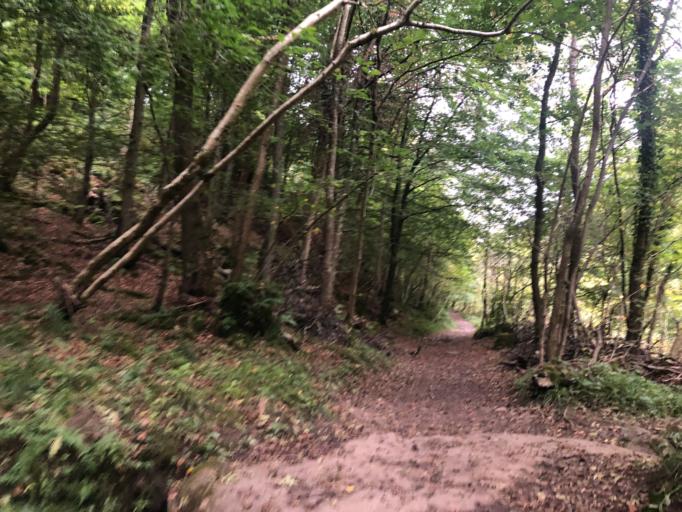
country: GB
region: Scotland
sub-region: Perth and Kinross
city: Pitlochry
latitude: 56.7393
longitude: -3.7723
